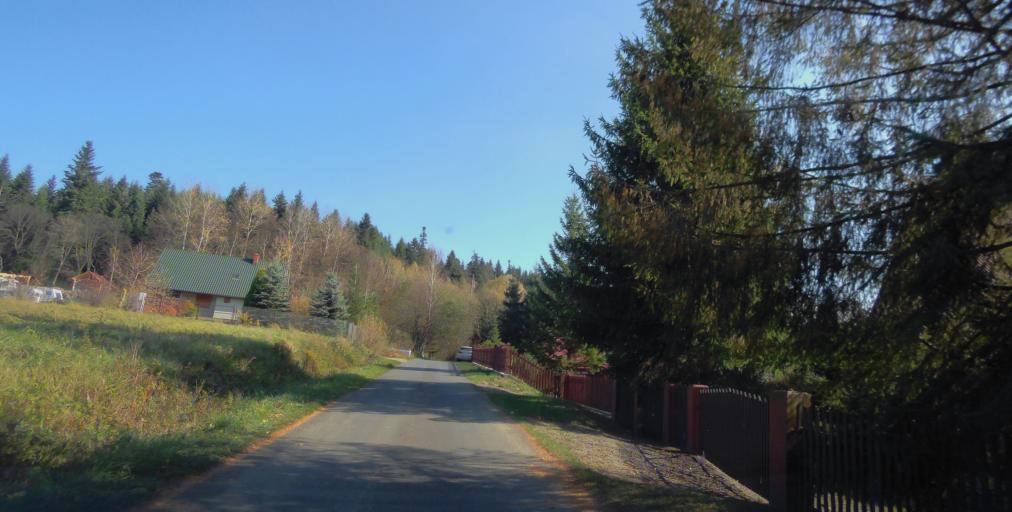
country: PL
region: Subcarpathian Voivodeship
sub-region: Powiat leski
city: Polanczyk
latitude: 49.3265
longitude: 22.4279
